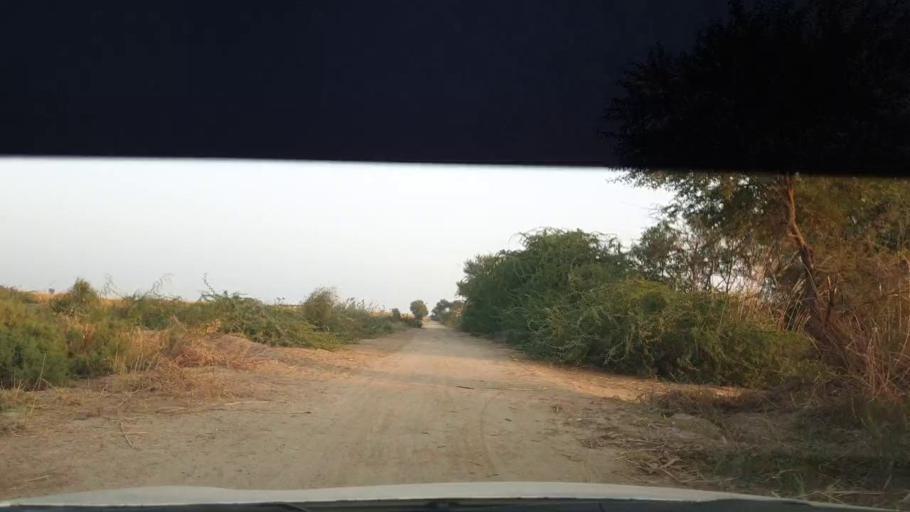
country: PK
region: Sindh
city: Berani
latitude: 25.7549
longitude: 69.0020
